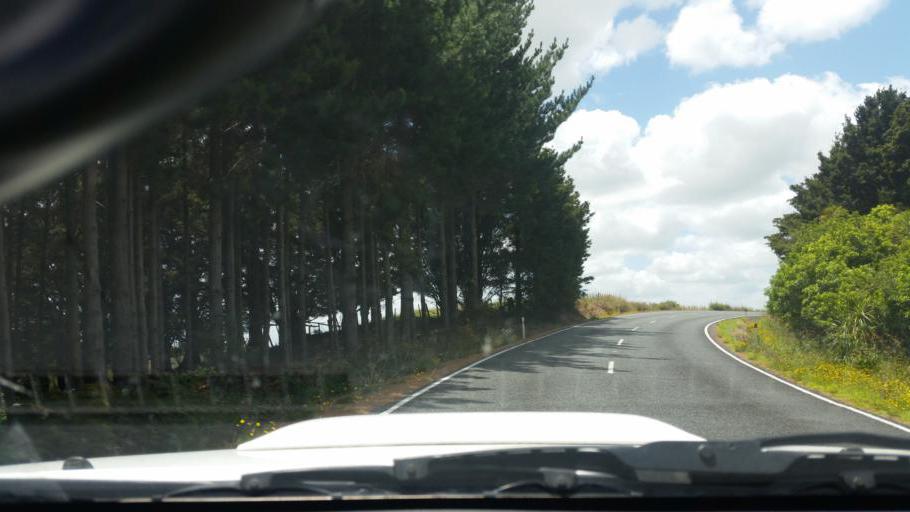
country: NZ
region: Northland
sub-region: Whangarei
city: Ruakaka
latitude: -36.0486
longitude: 174.2753
